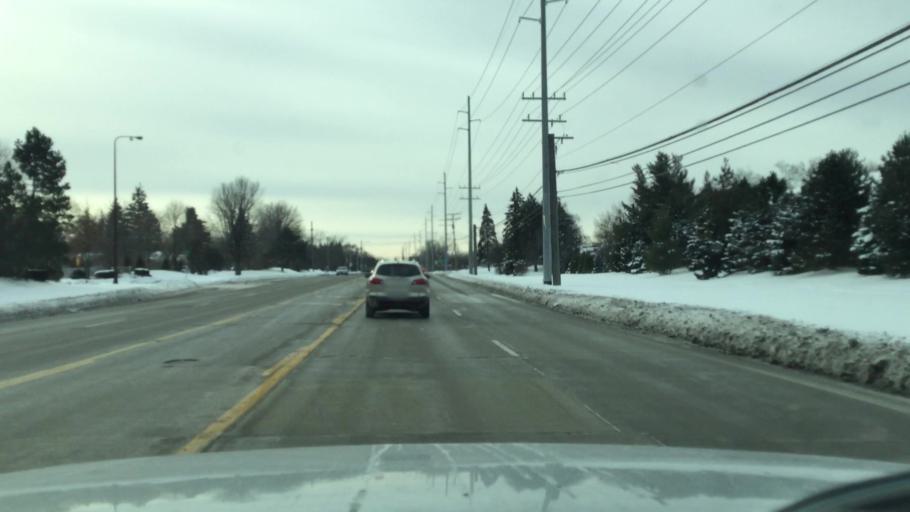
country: US
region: Michigan
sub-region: Oakland County
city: Troy
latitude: 42.6105
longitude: -83.1300
